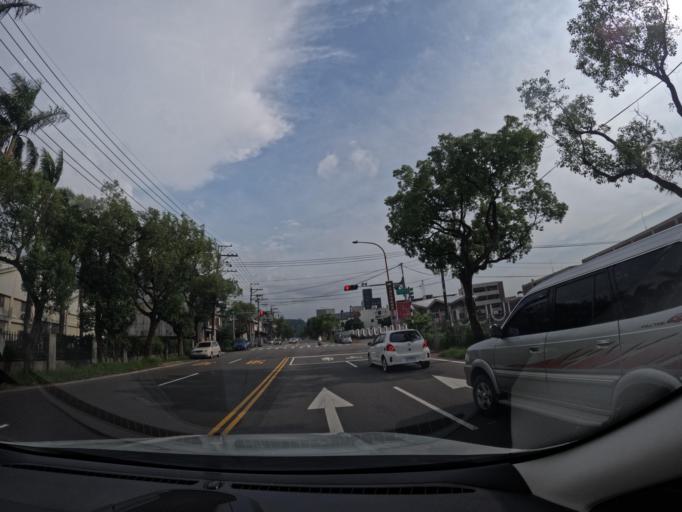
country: TW
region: Taiwan
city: Daxi
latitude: 24.8956
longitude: 121.3010
